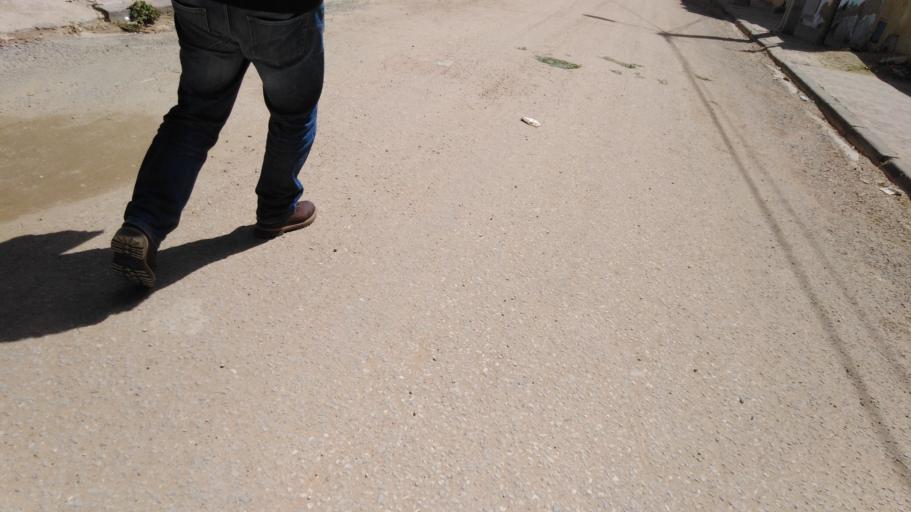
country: TN
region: Safaqis
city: Sfax
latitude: 34.7413
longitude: 10.5299
